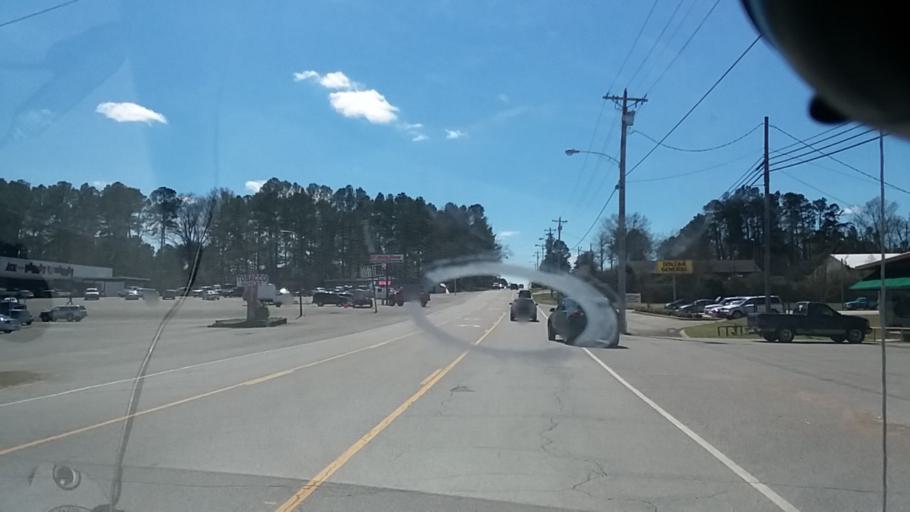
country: US
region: Mississippi
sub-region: Tishomingo County
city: Iuka
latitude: 34.8090
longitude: -88.1999
